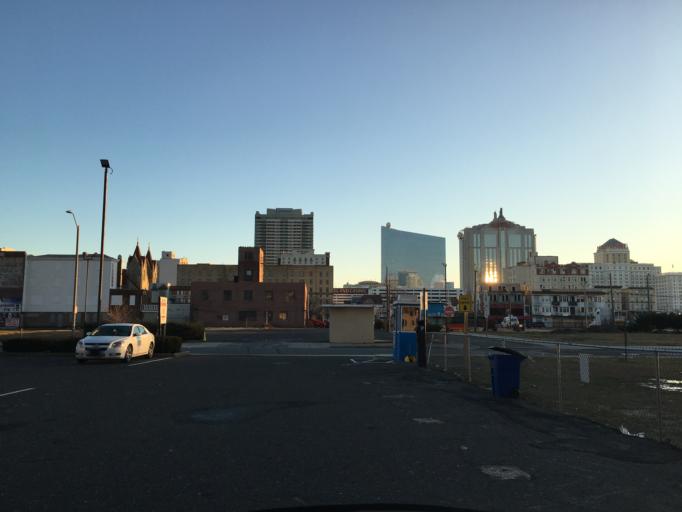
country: US
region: New Jersey
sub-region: Atlantic County
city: Atlantic City
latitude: 39.3592
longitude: -74.4296
